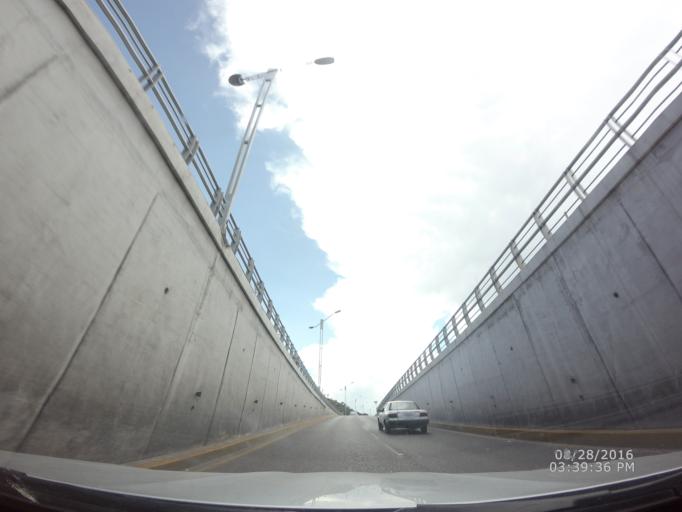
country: MX
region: Hidalgo
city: Pachuca de Soto
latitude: 20.1178
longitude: -98.7353
